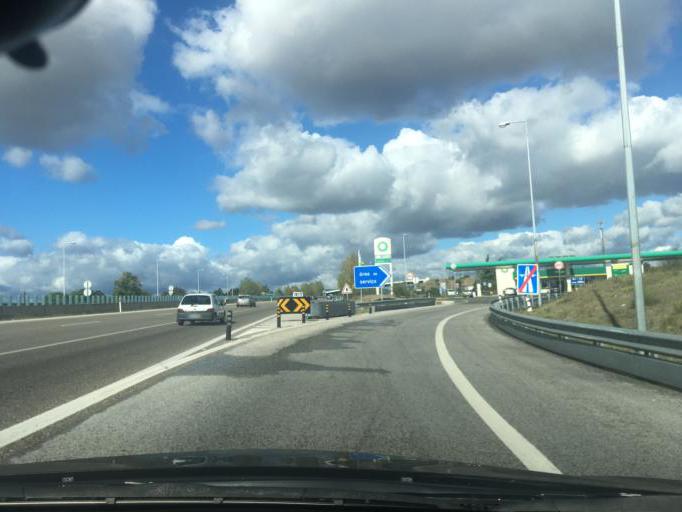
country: PT
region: Santarem
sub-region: Alcanena
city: Alcanena
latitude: 39.3903
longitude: -8.6380
